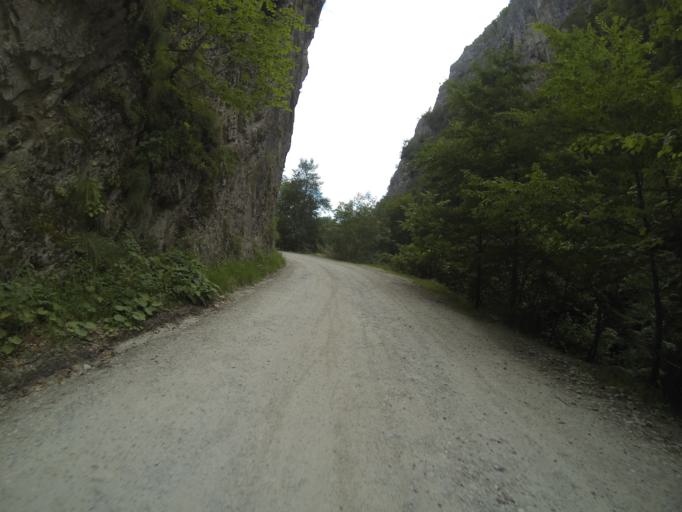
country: RO
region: Gorj
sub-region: Comuna Polovragi
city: Polovragi
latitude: 45.2003
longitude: 23.7840
